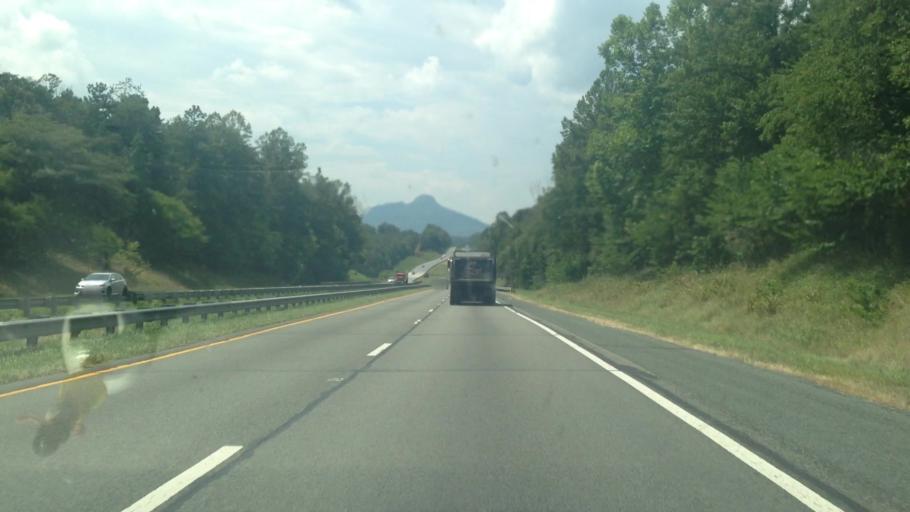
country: US
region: North Carolina
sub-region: Stokes County
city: King
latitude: 36.2979
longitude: -80.4097
